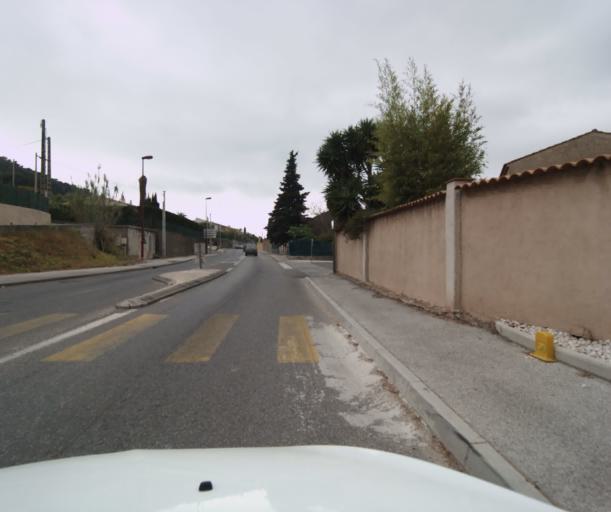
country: FR
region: Provence-Alpes-Cote d'Azur
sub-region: Departement du Var
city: Carqueiranne
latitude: 43.1192
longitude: 6.0727
